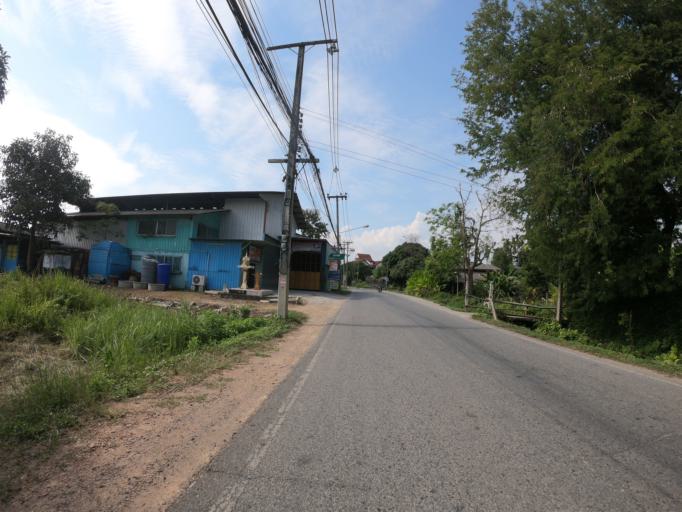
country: TH
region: Chiang Mai
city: San Sai
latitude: 18.8594
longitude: 99.0540
